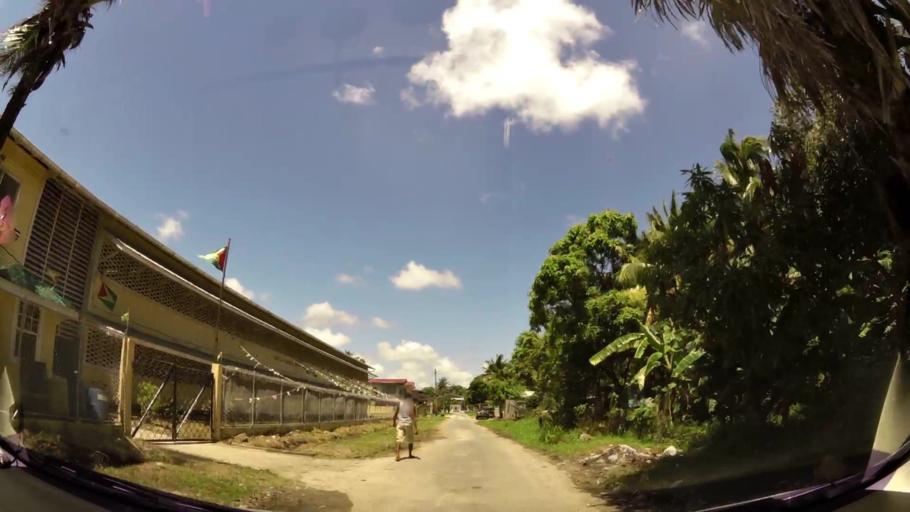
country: GY
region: Demerara-Mahaica
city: Georgetown
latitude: 6.7929
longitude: -58.1483
